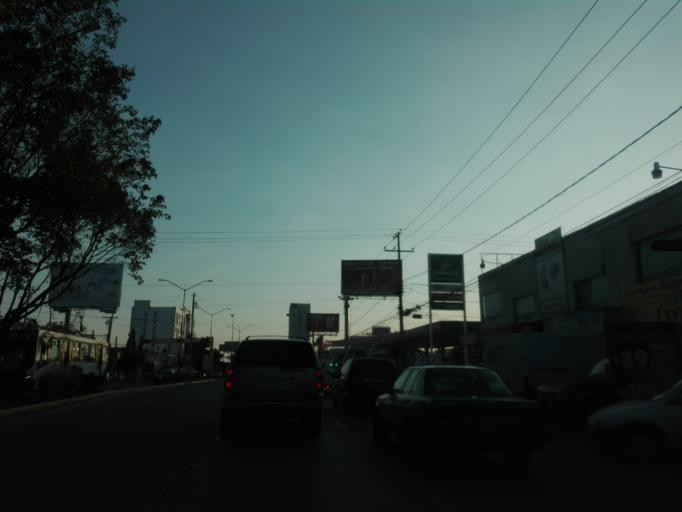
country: MX
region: Guanajuato
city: Leon
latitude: 21.1178
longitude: -101.6517
